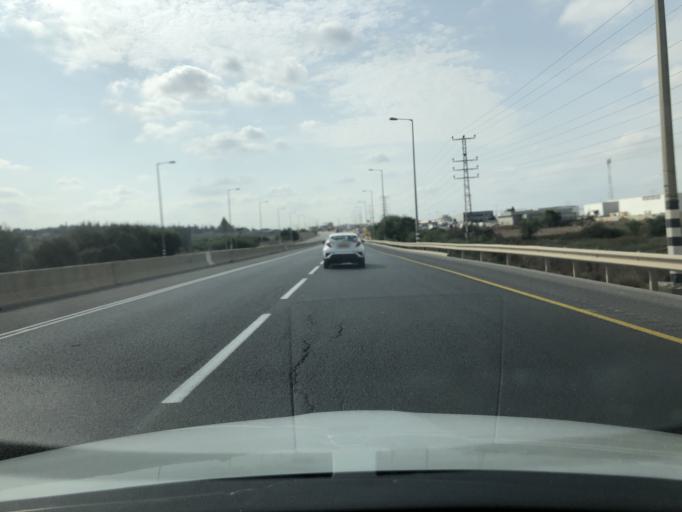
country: IL
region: Central District
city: Tirah
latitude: 32.2302
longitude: 34.9833
